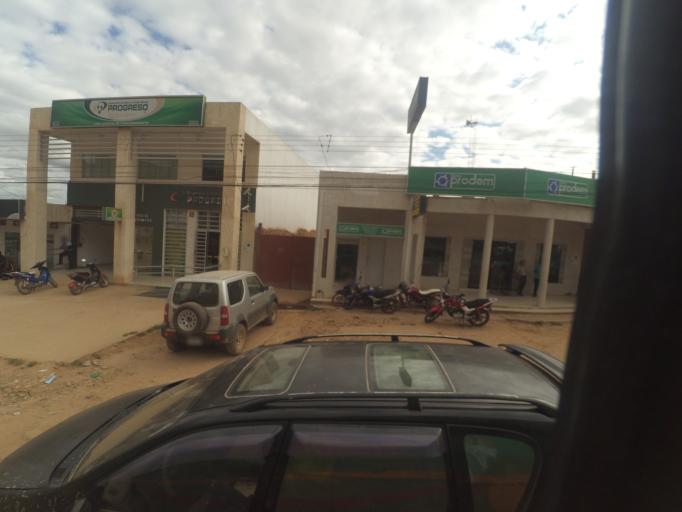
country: BO
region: Santa Cruz
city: Samaipata
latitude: -18.1636
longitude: -63.9248
